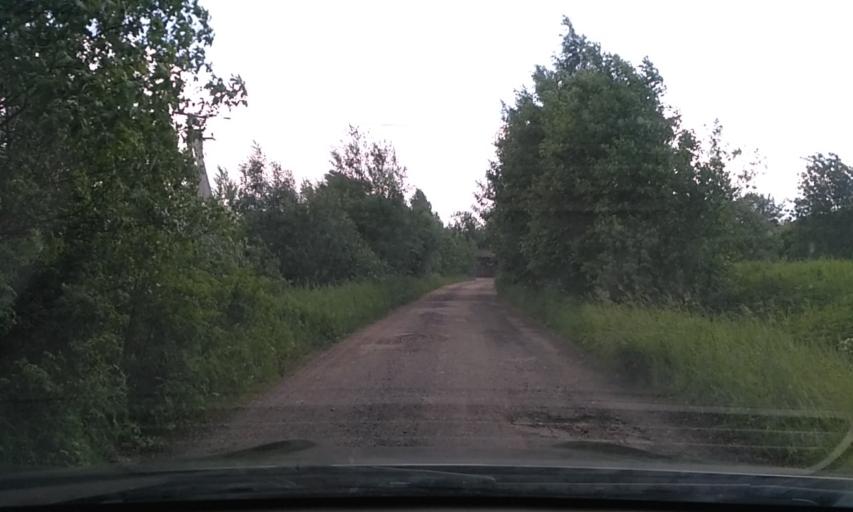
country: RU
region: Leningrad
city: Otradnoye
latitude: 59.8073
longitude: 30.8266
